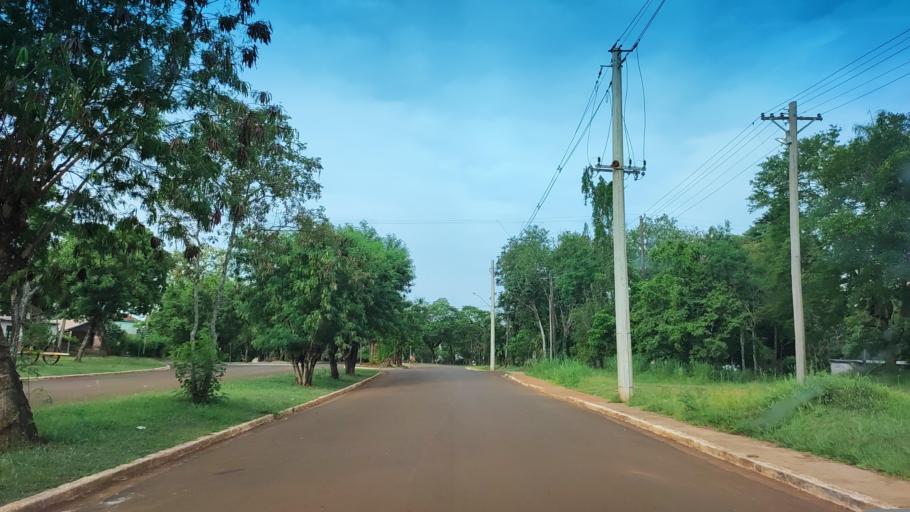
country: AR
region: Misiones
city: Gobernador Roca
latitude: -27.1310
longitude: -55.5119
